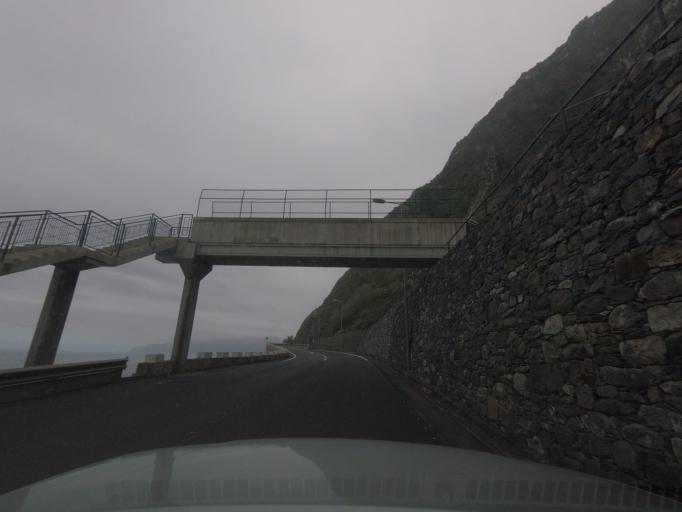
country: PT
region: Madeira
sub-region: Porto Moniz
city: Porto Moniz
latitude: 32.8591
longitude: -17.1606
